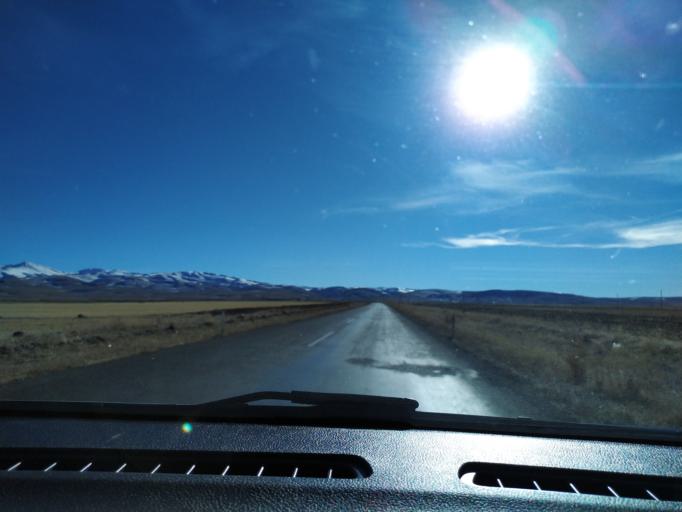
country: TR
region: Kayseri
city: Orensehir
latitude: 38.8865
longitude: 36.7286
